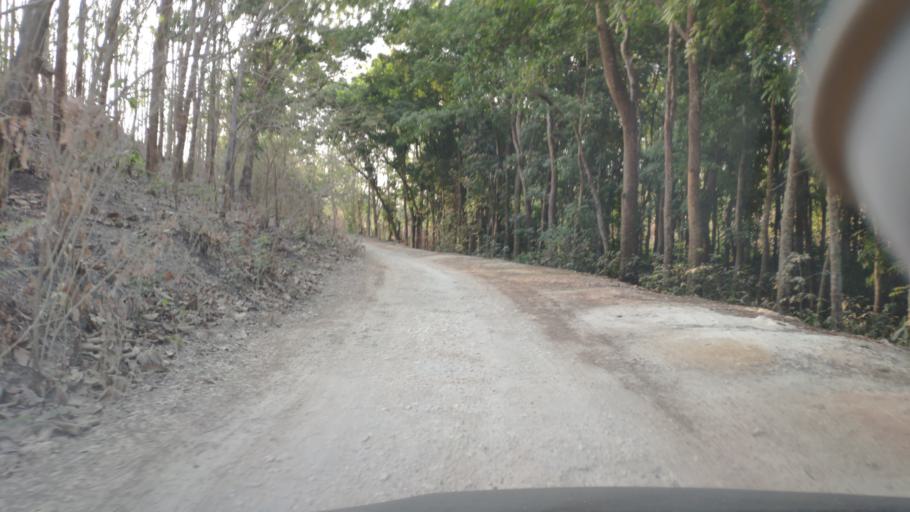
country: ID
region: Central Java
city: Sendangrejo
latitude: -6.9105
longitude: 111.5541
